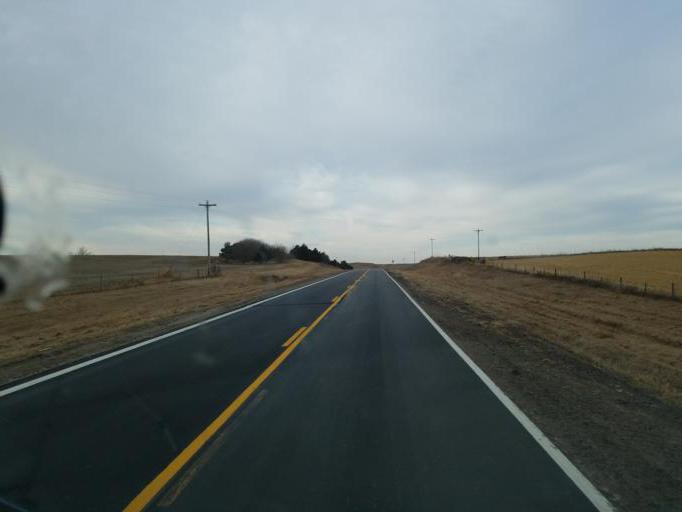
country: US
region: Nebraska
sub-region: Knox County
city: Center
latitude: 42.5970
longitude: -97.8115
